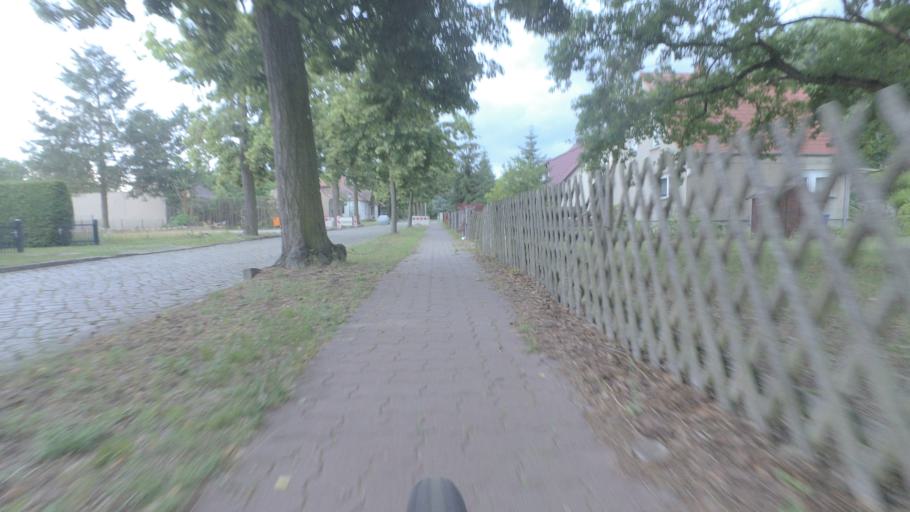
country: DE
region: Brandenburg
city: Bestensee
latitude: 52.2274
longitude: 13.6590
